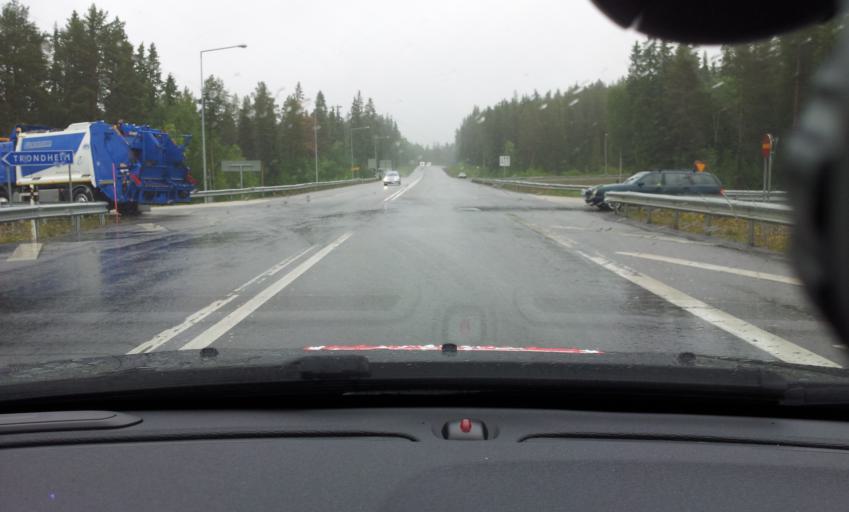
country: SE
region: Jaemtland
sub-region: OEstersunds Kommun
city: Ostersund
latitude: 63.2031
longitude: 14.6778
